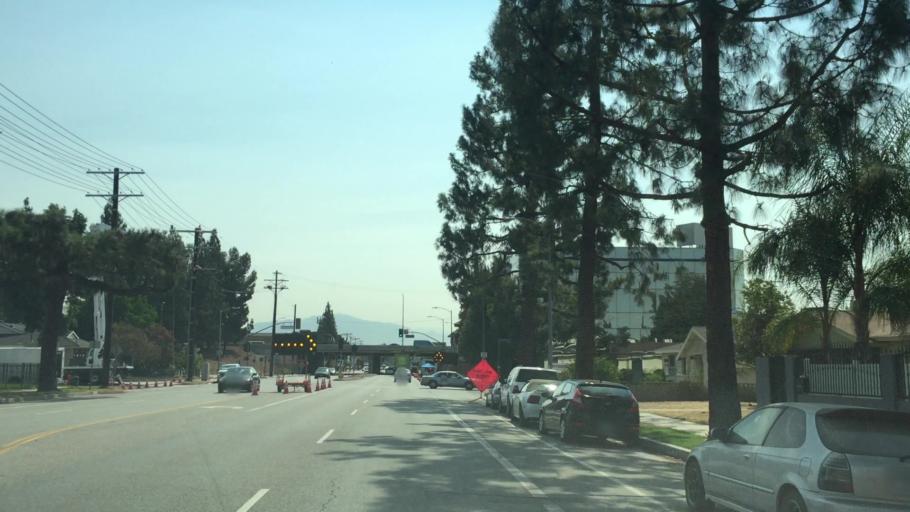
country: US
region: California
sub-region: Los Angeles County
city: San Fernando
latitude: 34.2573
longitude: -118.4747
